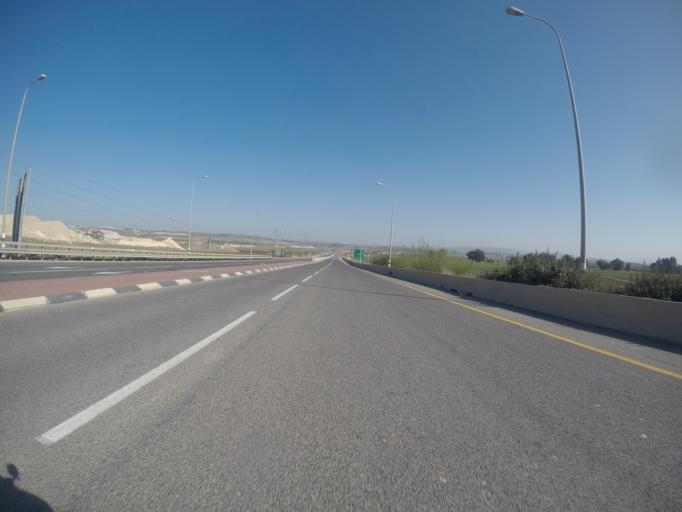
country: IL
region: Haifa
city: Daliyat el Karmil
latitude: 32.6735
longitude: 35.1099
